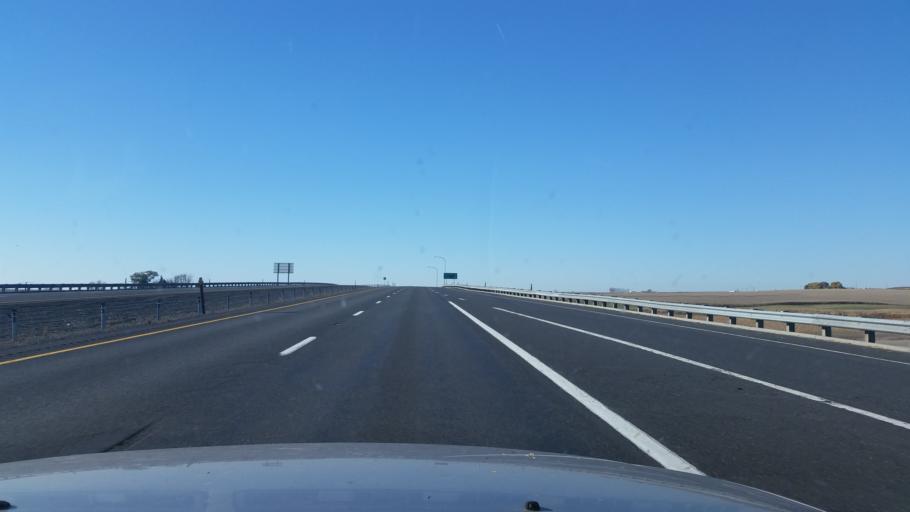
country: US
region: Washington
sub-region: Grant County
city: Warden
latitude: 47.0859
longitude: -119.0482
